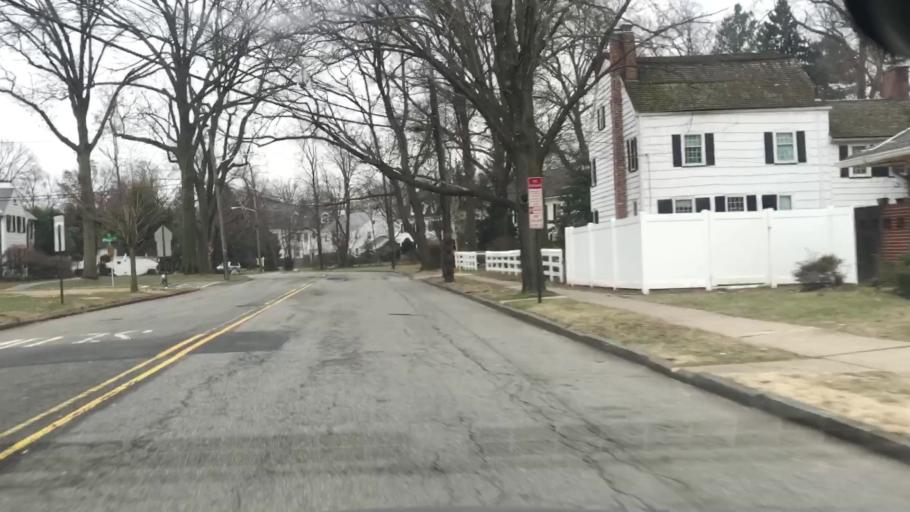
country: US
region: New Jersey
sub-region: Union County
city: Hillside
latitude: 40.6841
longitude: -74.2188
